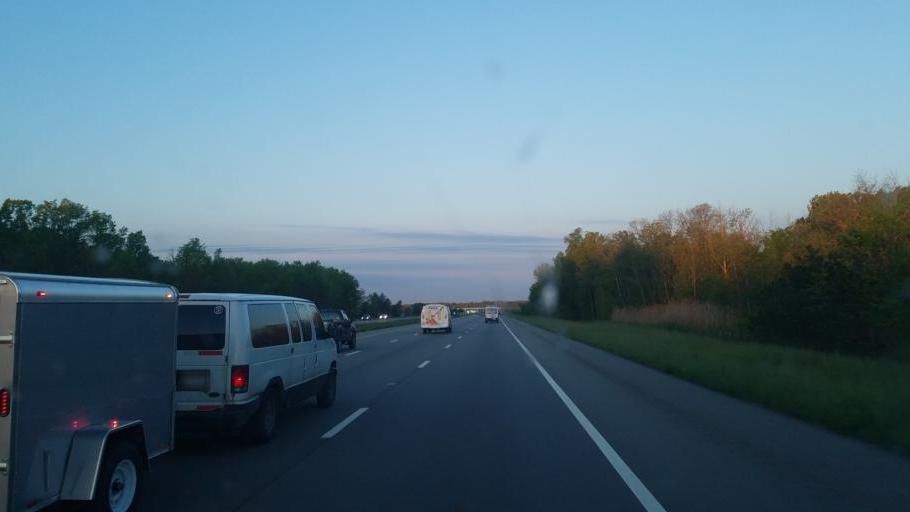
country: US
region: Ohio
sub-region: Delaware County
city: Sunbury
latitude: 40.3235
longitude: -82.9012
